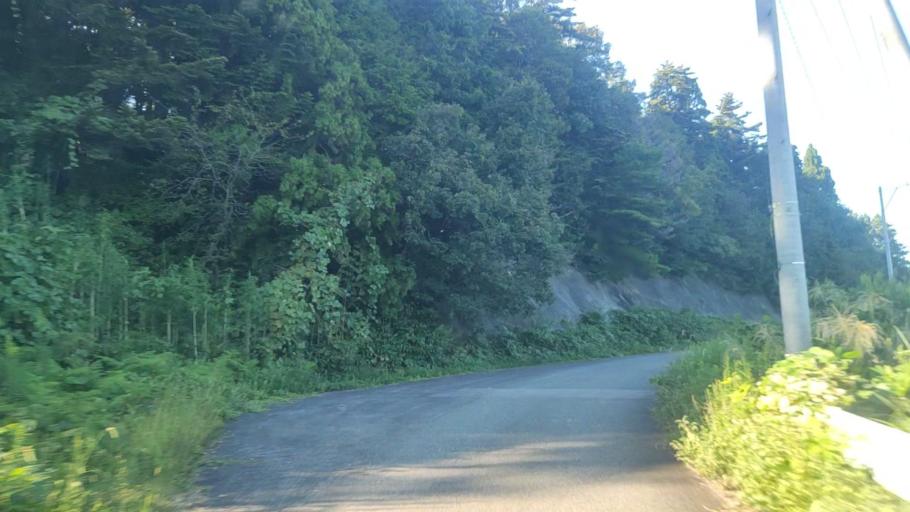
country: JP
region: Ishikawa
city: Nanao
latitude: 37.1259
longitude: 136.8958
